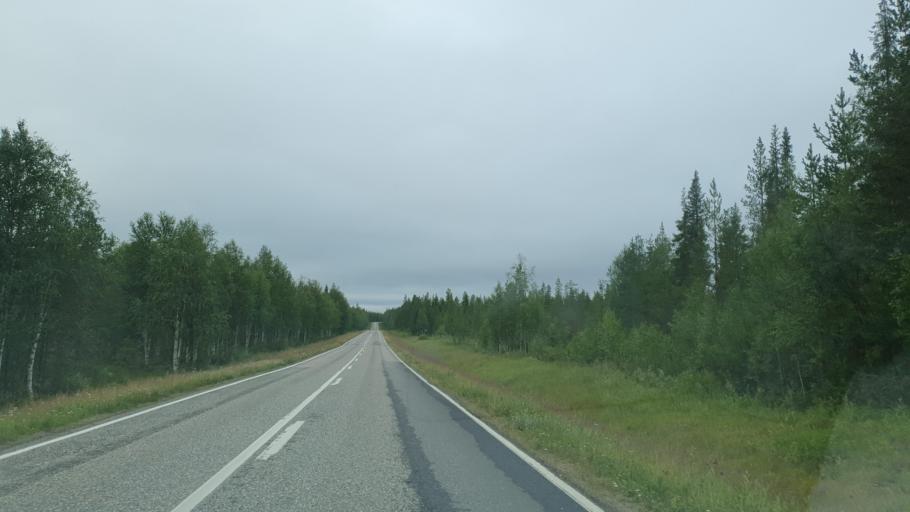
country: FI
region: Lapland
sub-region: Itae-Lappi
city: Pyhaejaervi
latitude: 67.3526
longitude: 27.0142
